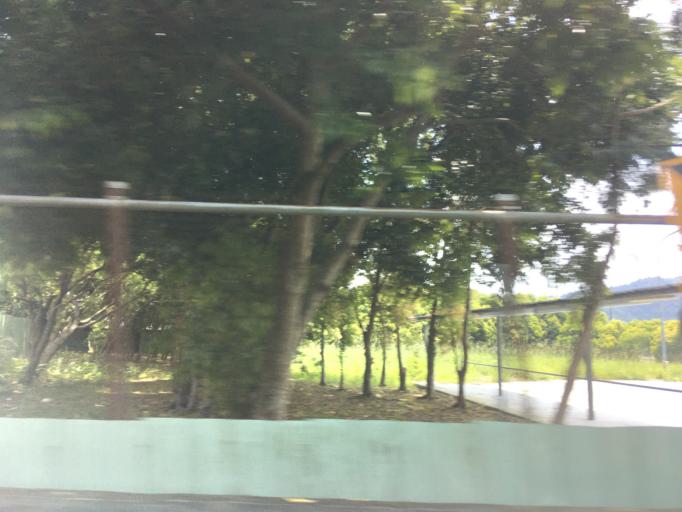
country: TW
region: Taiwan
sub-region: Yilan
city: Yilan
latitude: 24.8212
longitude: 121.7551
